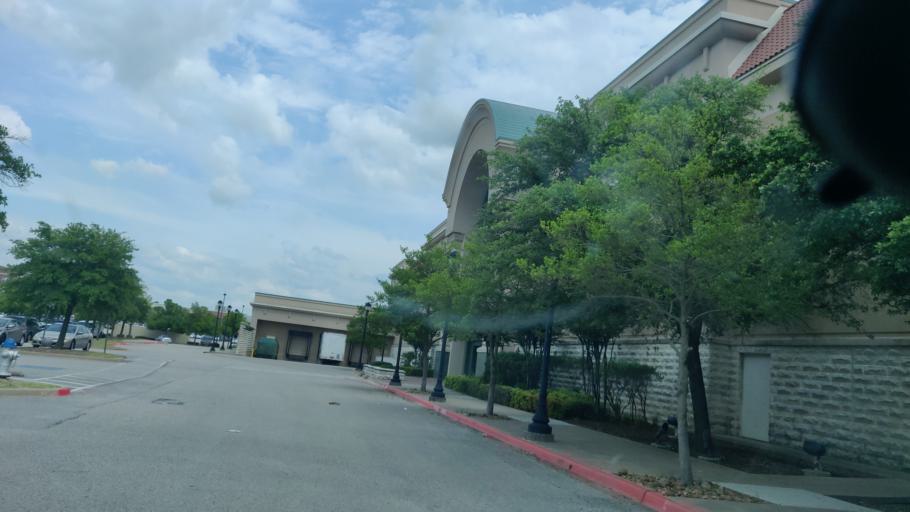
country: US
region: Texas
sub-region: Dallas County
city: Sachse
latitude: 32.9554
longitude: -96.6150
